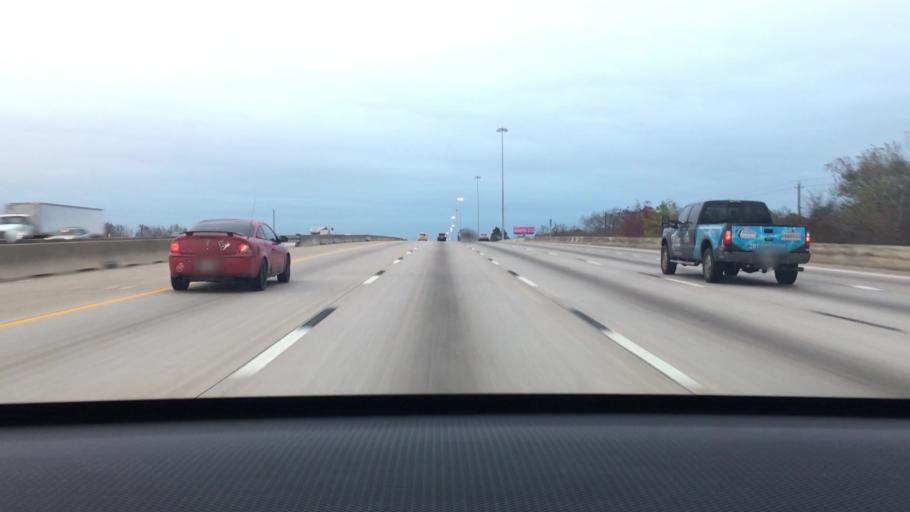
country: US
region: Texas
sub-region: Harris County
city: Aldine
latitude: 29.8777
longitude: -95.3256
